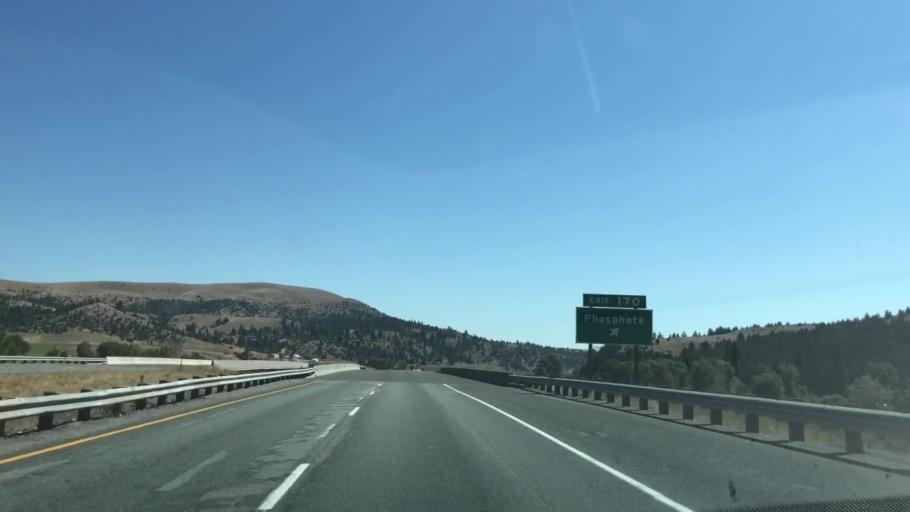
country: US
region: Montana
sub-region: Powell County
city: Deer Lodge
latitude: 46.5571
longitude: -112.8744
